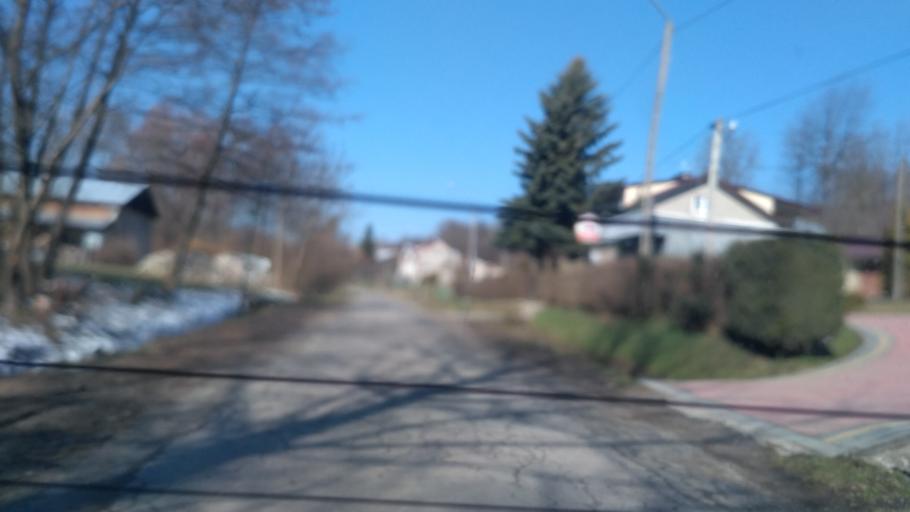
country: PL
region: Subcarpathian Voivodeship
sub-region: Powiat strzyzowski
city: Gwoznica Gorna
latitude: 49.8166
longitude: 22.0252
